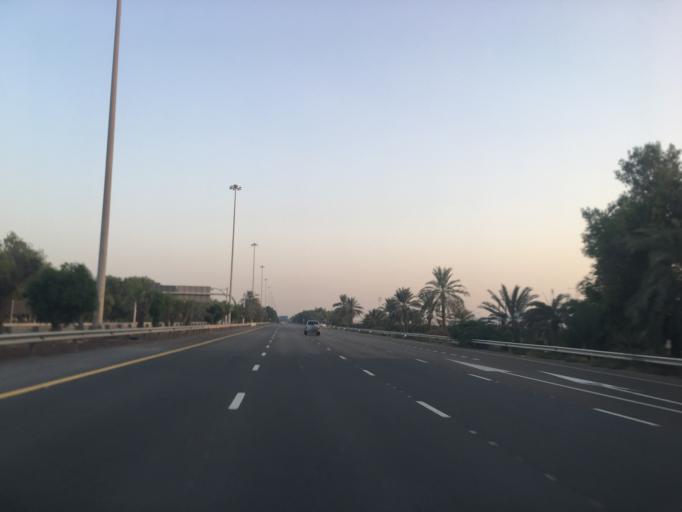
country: AE
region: Abu Dhabi
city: Abu Dhabi
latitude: 24.3369
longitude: 54.5794
